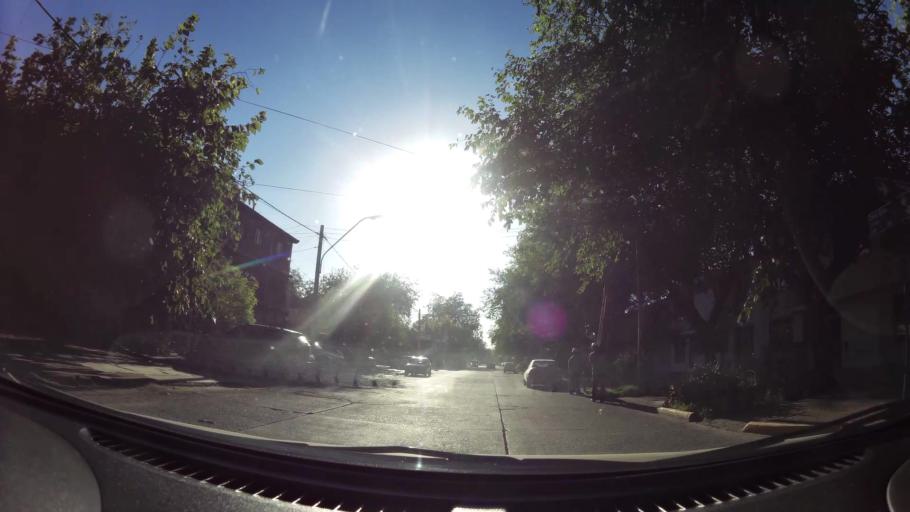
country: AR
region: Mendoza
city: Las Heras
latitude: -32.8664
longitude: -68.8253
